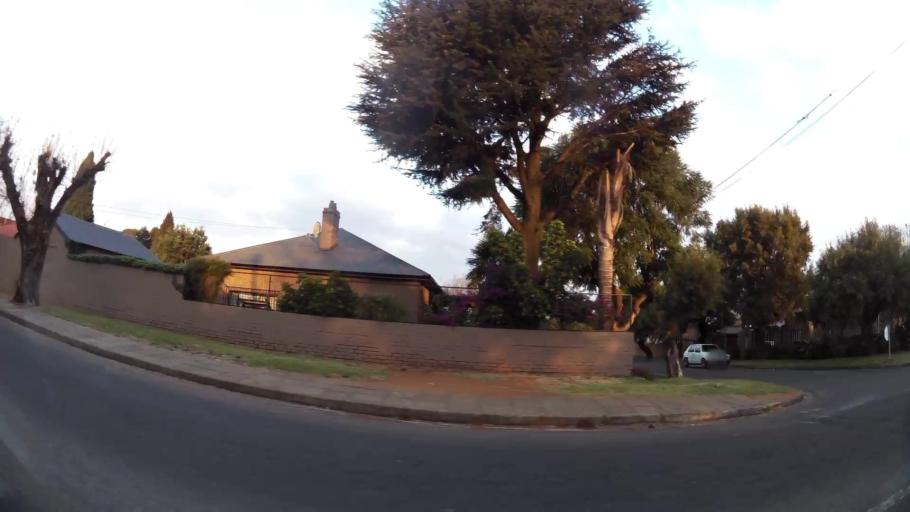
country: ZA
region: Gauteng
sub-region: Ekurhuleni Metropolitan Municipality
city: Germiston
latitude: -26.1881
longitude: 28.1568
